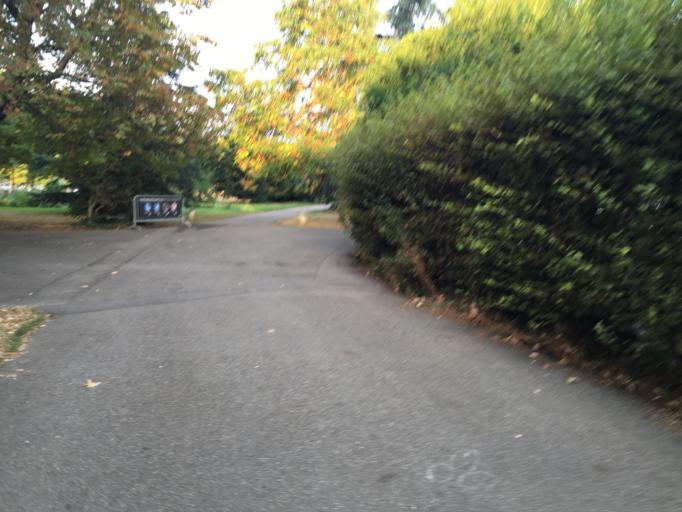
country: CH
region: Geneva
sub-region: Geneva
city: Geneve
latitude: 46.2153
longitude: 6.1380
